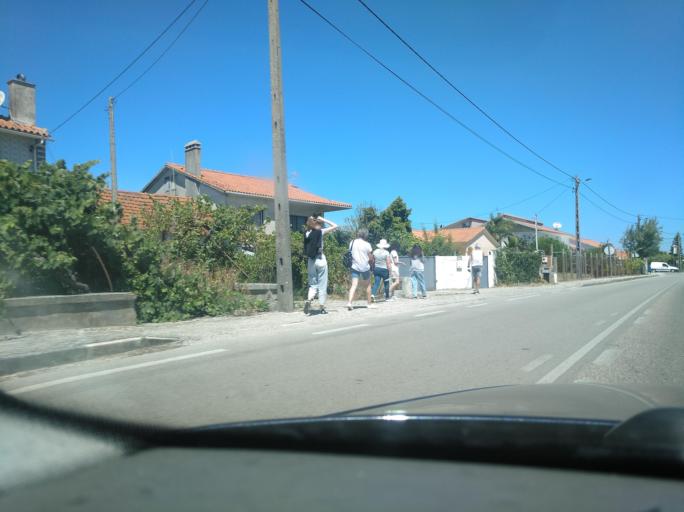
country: PT
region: Leiria
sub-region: Alcobaca
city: Aljubarrota
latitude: 39.5757
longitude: -8.9140
